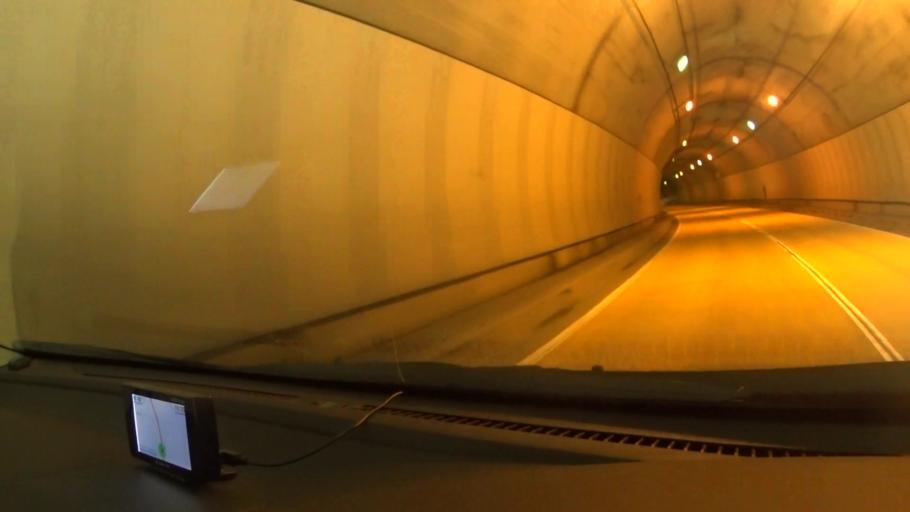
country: JP
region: Kyoto
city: Ayabe
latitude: 35.2690
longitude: 135.2705
